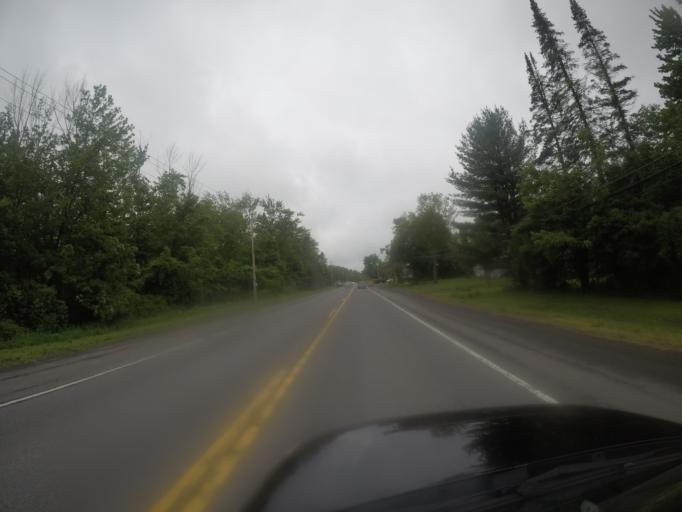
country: US
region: New York
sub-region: Ulster County
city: Shokan
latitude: 41.9761
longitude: -74.1953
